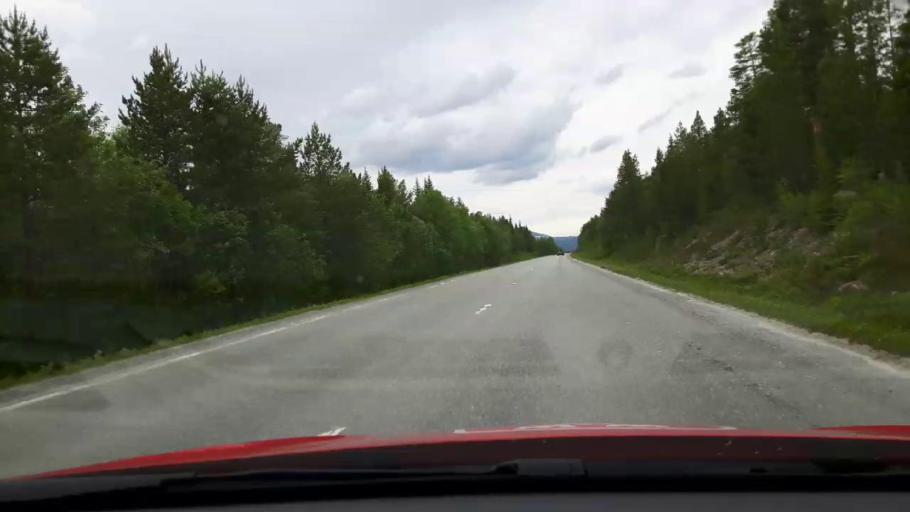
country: NO
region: Hedmark
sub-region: Engerdal
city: Engerdal
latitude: 62.5263
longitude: 12.5801
